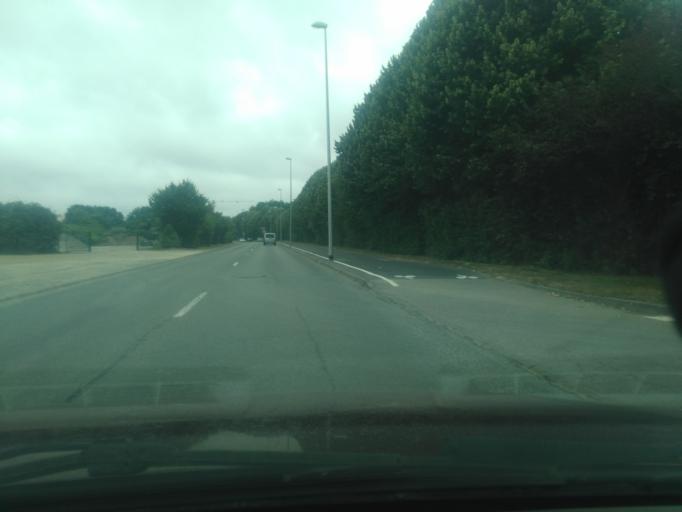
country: FR
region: Pays de la Loire
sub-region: Departement de la Vendee
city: La Roche-sur-Yon
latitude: 46.6843
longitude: -1.4343
